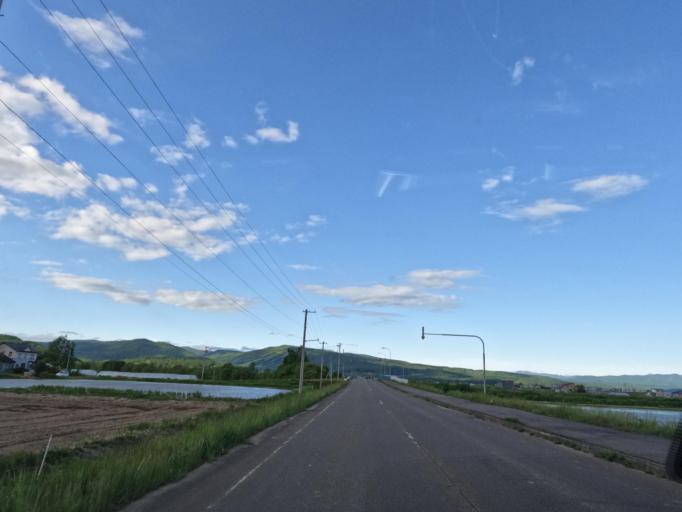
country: JP
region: Hokkaido
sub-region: Asahikawa-shi
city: Asahikawa
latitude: 43.8869
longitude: 142.4616
